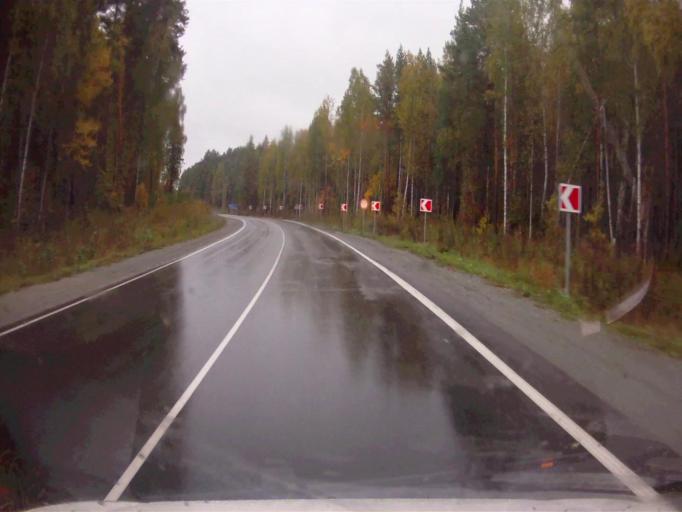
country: RU
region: Chelyabinsk
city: Tayginka
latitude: 55.6344
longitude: 60.5990
